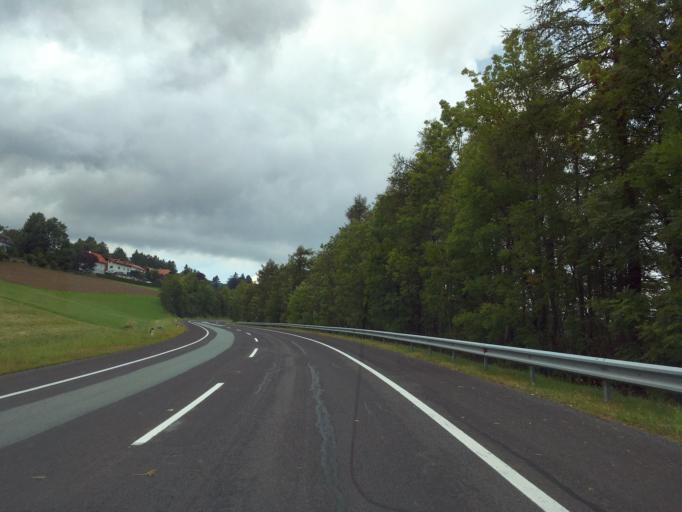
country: AT
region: Lower Austria
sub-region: Politischer Bezirk Neunkirchen
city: Monichkirchen
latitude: 47.4915
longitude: 16.0415
